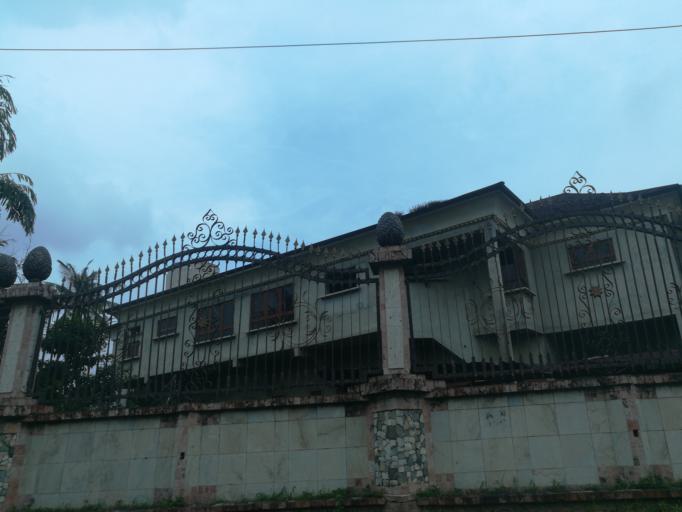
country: NG
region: Lagos
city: Oshodi
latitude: 6.5736
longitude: 3.3465
